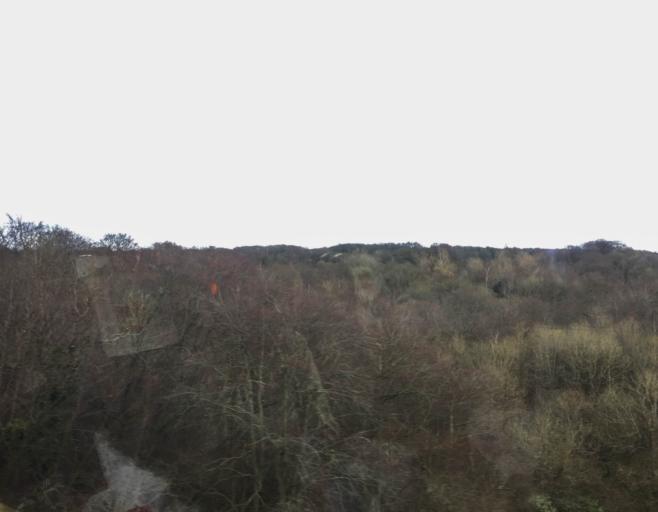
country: GB
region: Scotland
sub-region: North Lanarkshire
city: Newarthill
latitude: 55.7942
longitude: -3.9508
